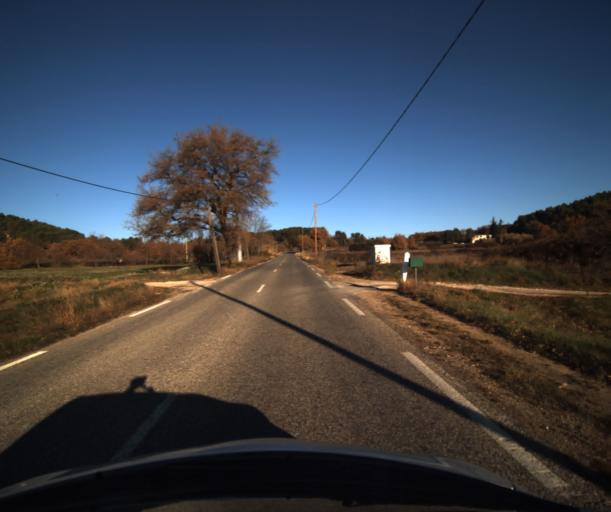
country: FR
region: Provence-Alpes-Cote d'Azur
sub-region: Departement du Vaucluse
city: Pertuis
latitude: 43.7130
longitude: 5.4943
